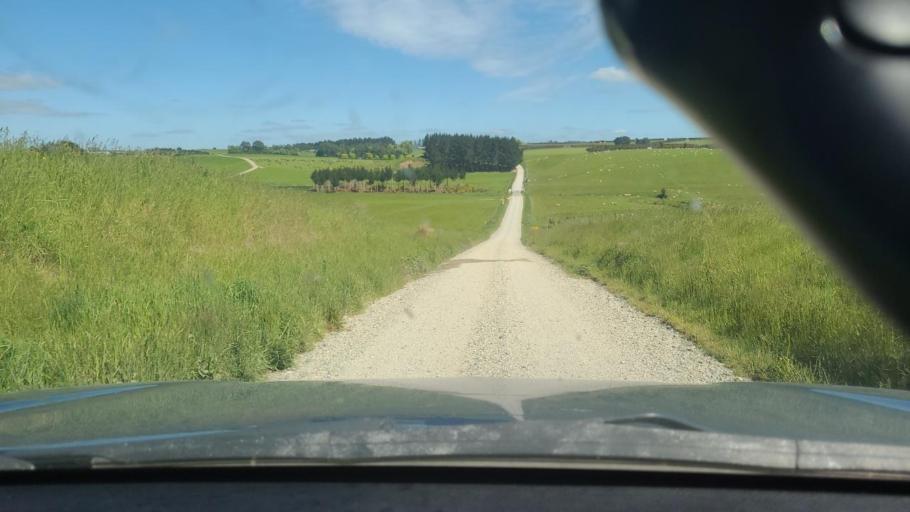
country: NZ
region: Southland
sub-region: Gore District
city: Gore
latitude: -46.3356
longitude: 168.9157
